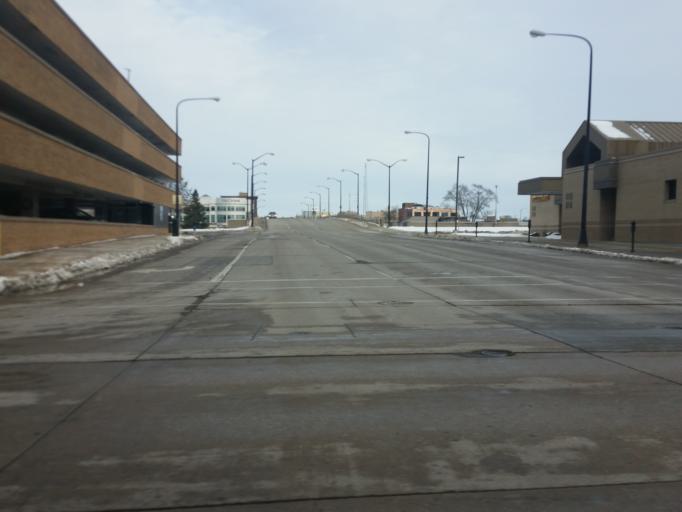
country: US
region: Iowa
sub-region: Black Hawk County
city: Waterloo
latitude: 42.4944
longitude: -92.3387
